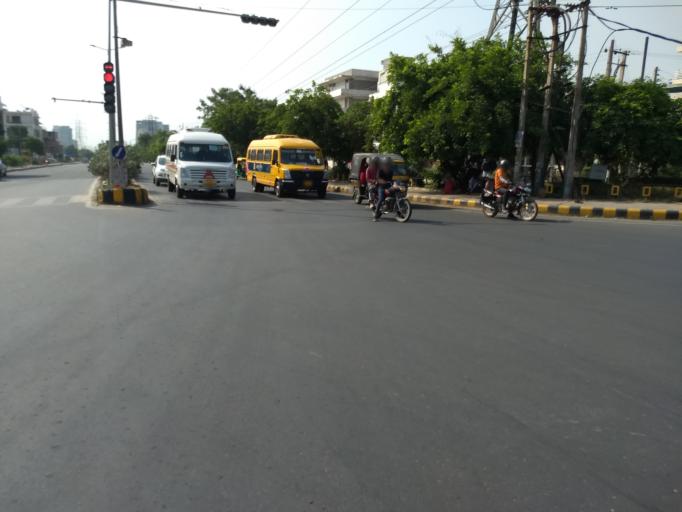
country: IN
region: Haryana
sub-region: Gurgaon
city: Gurgaon
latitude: 28.4348
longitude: 77.0491
